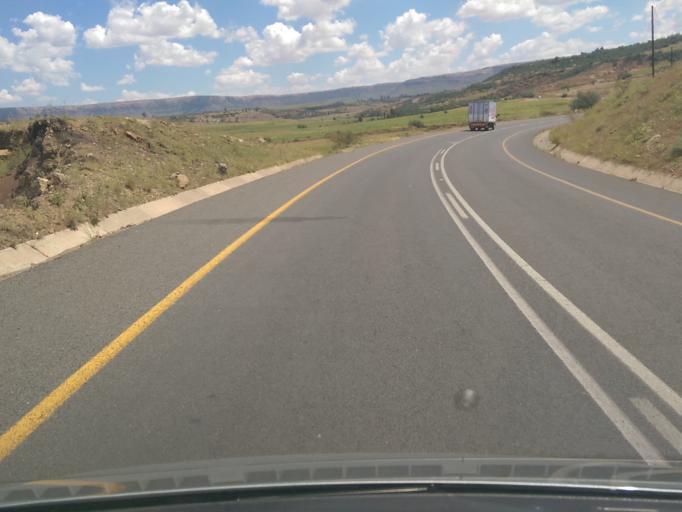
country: LS
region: Maseru
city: Maseru
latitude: -29.3921
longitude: 27.5472
